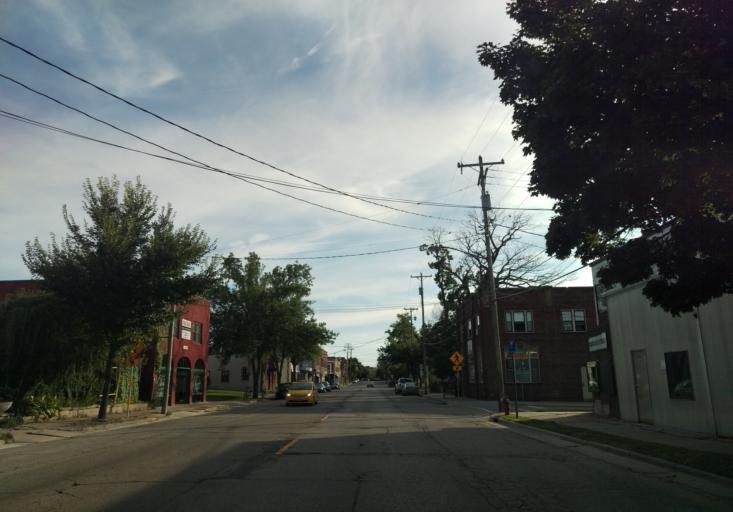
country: US
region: Wisconsin
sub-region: Dane County
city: Maple Bluff
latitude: 43.0935
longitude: -89.3540
